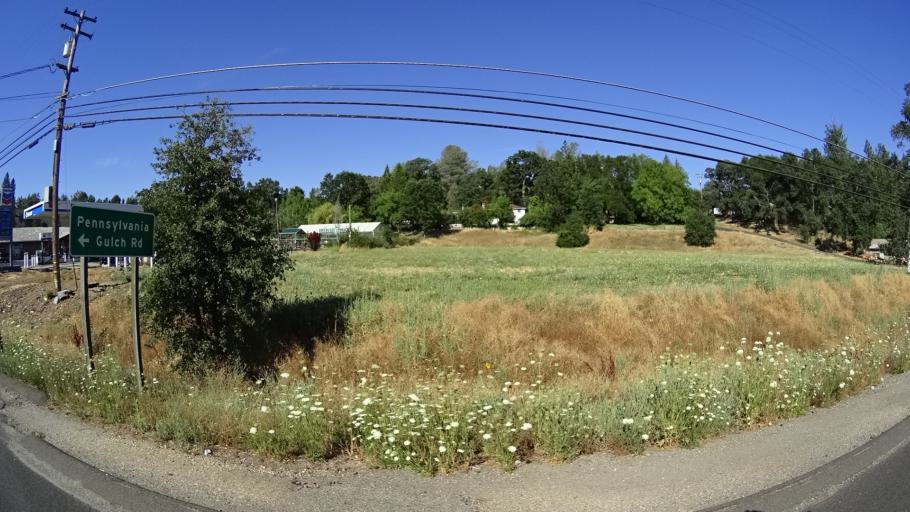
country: US
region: California
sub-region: Calaveras County
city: Murphys
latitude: 38.1348
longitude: -120.4559
